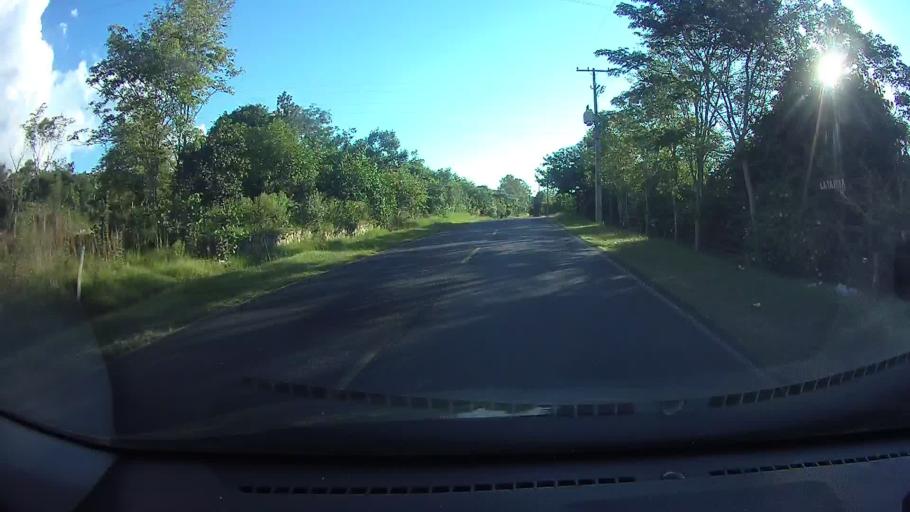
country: PY
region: Cordillera
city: Emboscada
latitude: -25.1800
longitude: -57.2928
